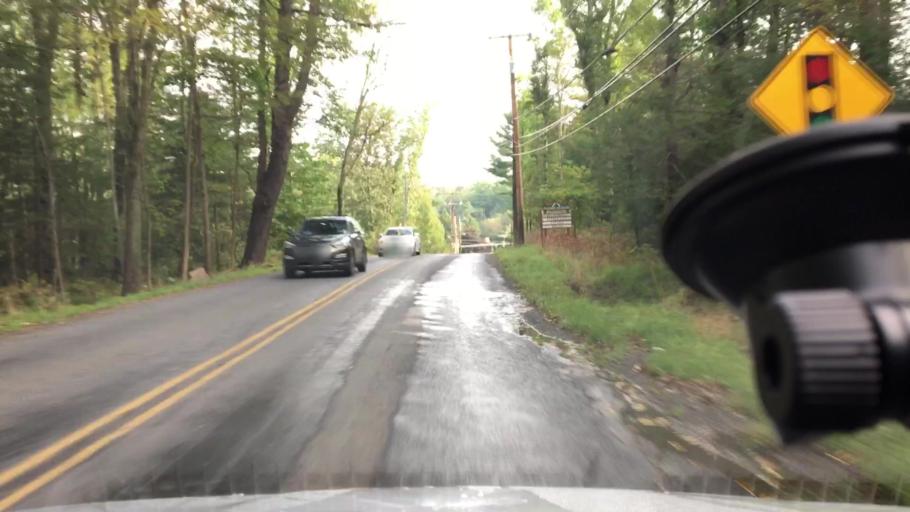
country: US
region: Pennsylvania
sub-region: Monroe County
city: Mount Pocono
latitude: 41.1256
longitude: -75.3110
